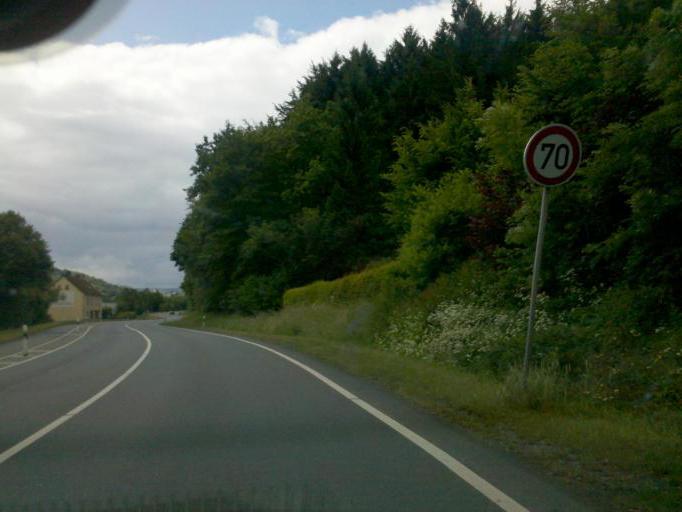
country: DE
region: North Rhine-Westphalia
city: Warstein
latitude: 51.4731
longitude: 8.3388
